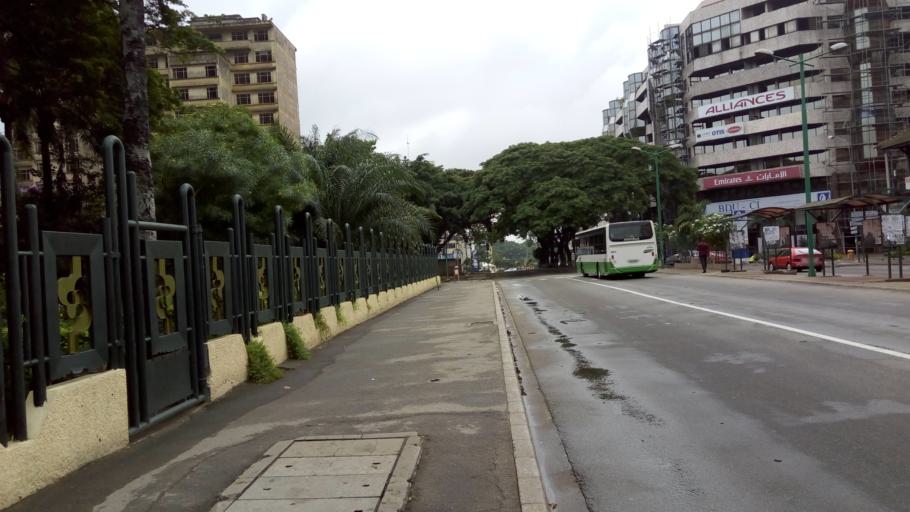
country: CI
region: Lagunes
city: Abidjan
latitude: 5.3236
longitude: -4.0198
